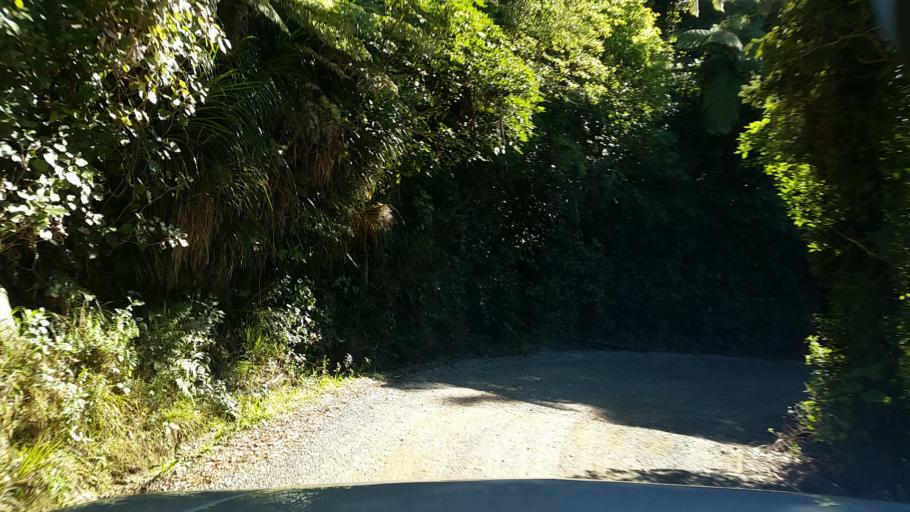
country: NZ
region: Marlborough
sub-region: Marlborough District
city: Picton
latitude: -41.1053
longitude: 173.6548
